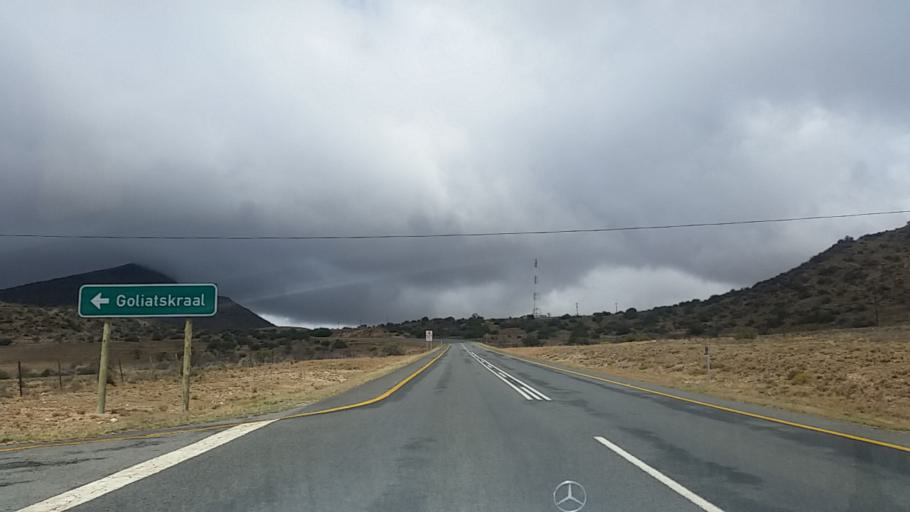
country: ZA
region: Eastern Cape
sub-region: Cacadu District Municipality
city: Graaff-Reinet
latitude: -32.1034
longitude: 24.6059
